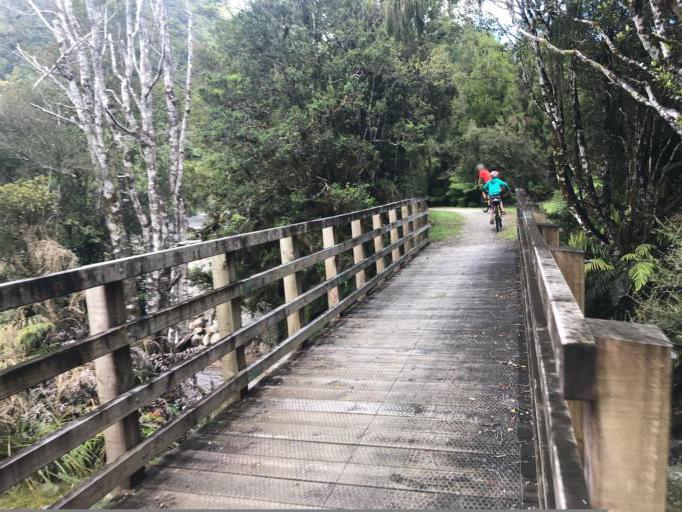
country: NZ
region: West Coast
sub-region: Westland District
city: Hokitika
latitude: -42.7599
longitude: 171.2415
